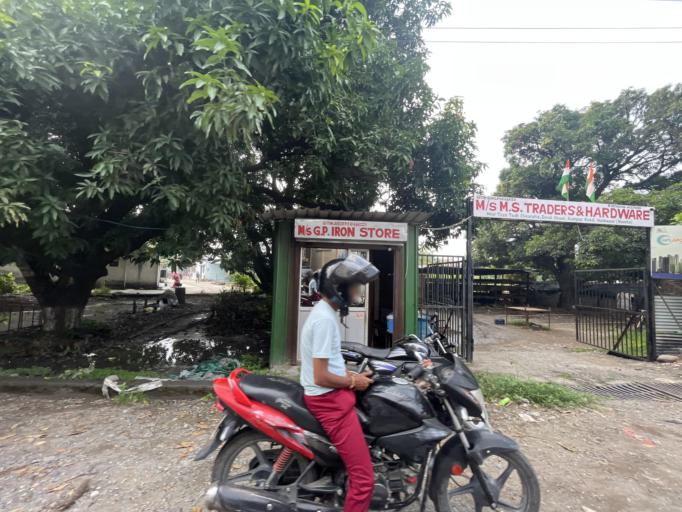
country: IN
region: Uttarakhand
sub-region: Naini Tal
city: Haldwani
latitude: 29.1942
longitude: 79.4991
